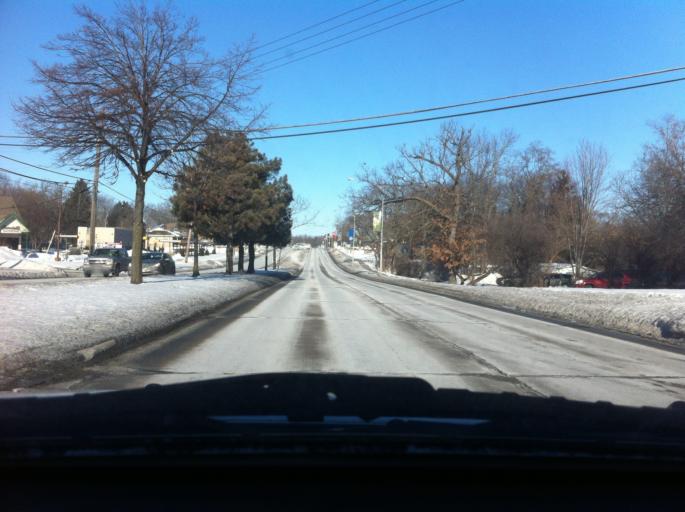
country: US
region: Wisconsin
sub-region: Dane County
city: Middleton
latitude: 43.0924
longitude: -89.4898
